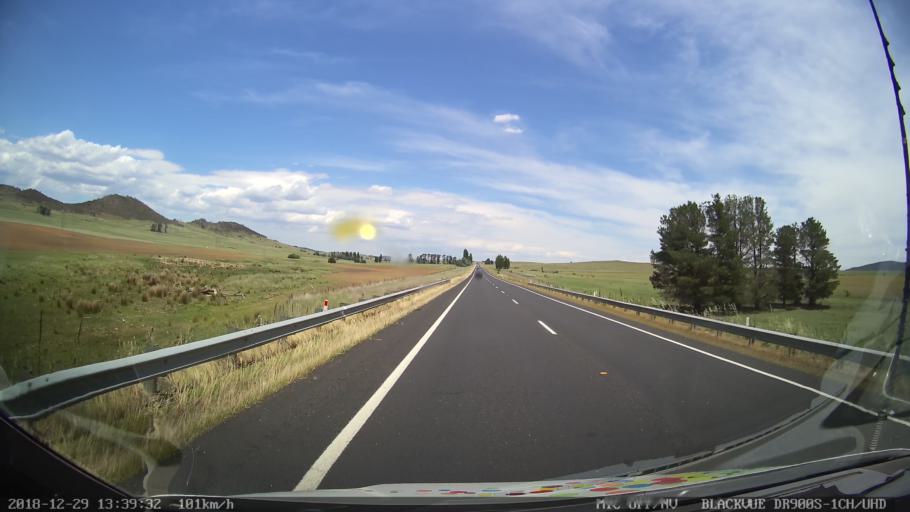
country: AU
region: New South Wales
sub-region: Cooma-Monaro
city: Cooma
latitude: -36.0144
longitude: 149.1475
